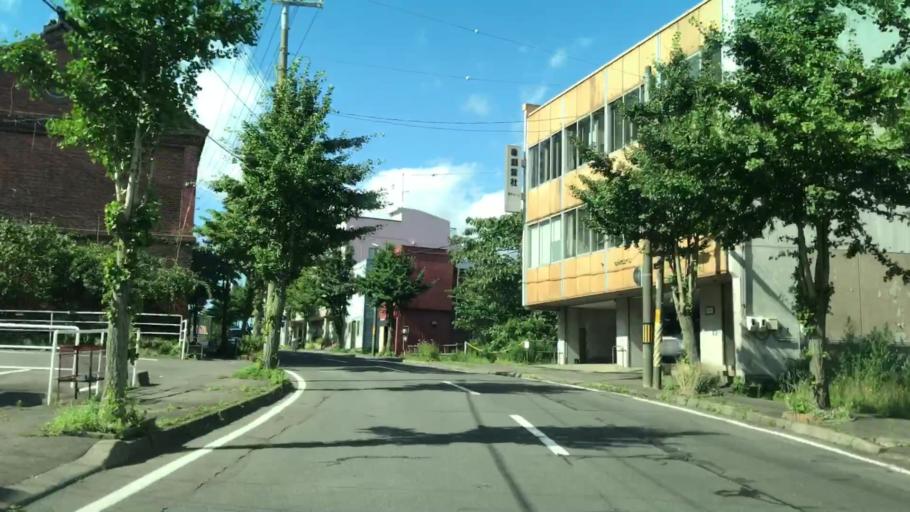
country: JP
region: Hokkaido
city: Muroran
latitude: 42.3203
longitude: 140.9705
